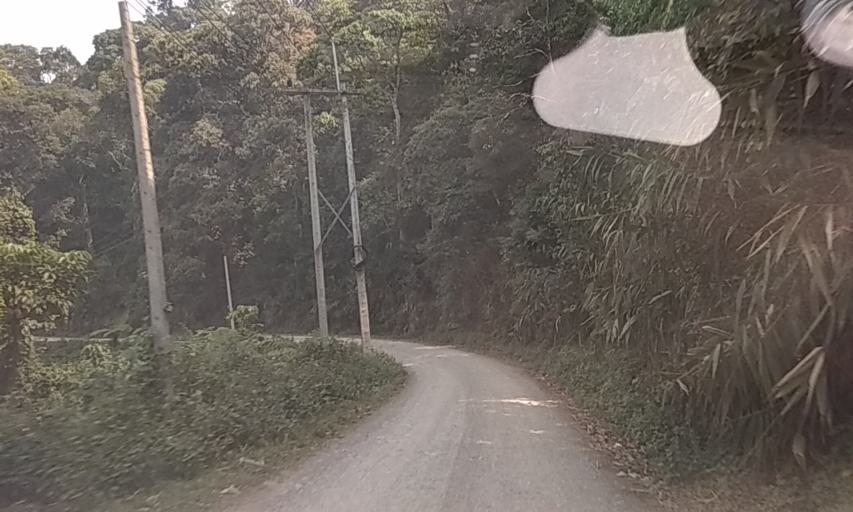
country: TH
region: Nan
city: Chaloem Phra Kiat
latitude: 20.0382
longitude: 101.0959
